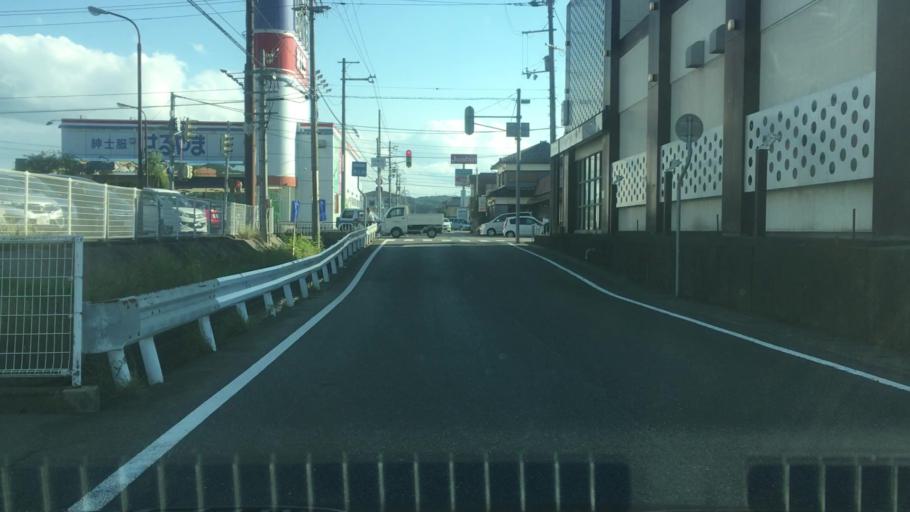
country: JP
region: Hyogo
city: Toyooka
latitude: 35.5547
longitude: 134.8130
